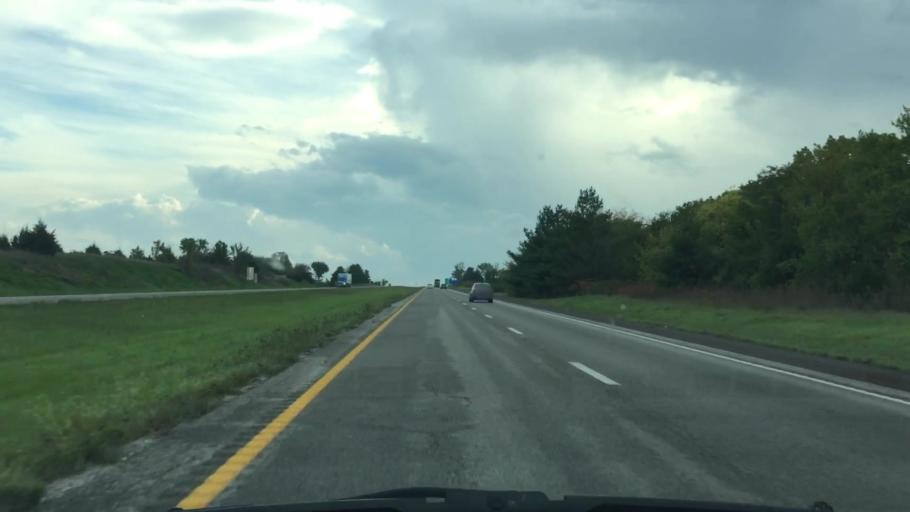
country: US
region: Missouri
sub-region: Clinton County
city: Cameron
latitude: 39.8646
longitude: -94.1720
